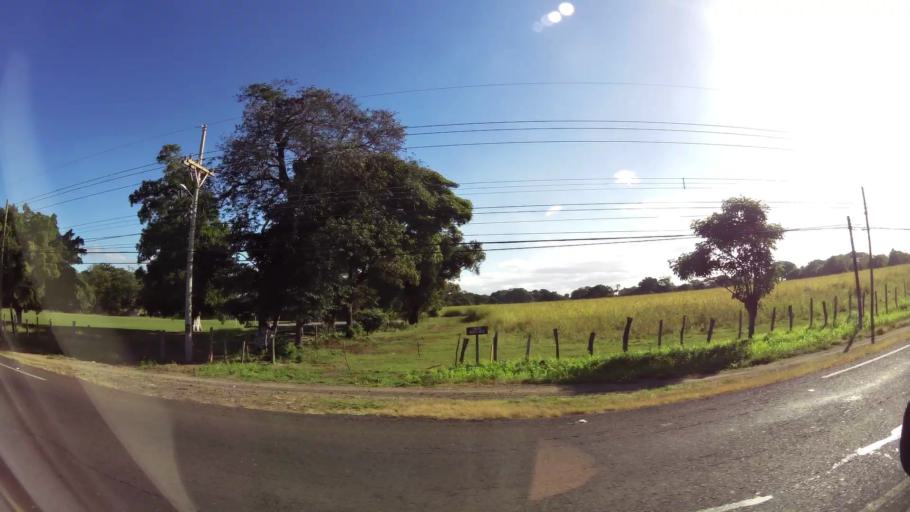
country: CR
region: Guanacaste
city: Belen
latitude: 10.4767
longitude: -85.5638
